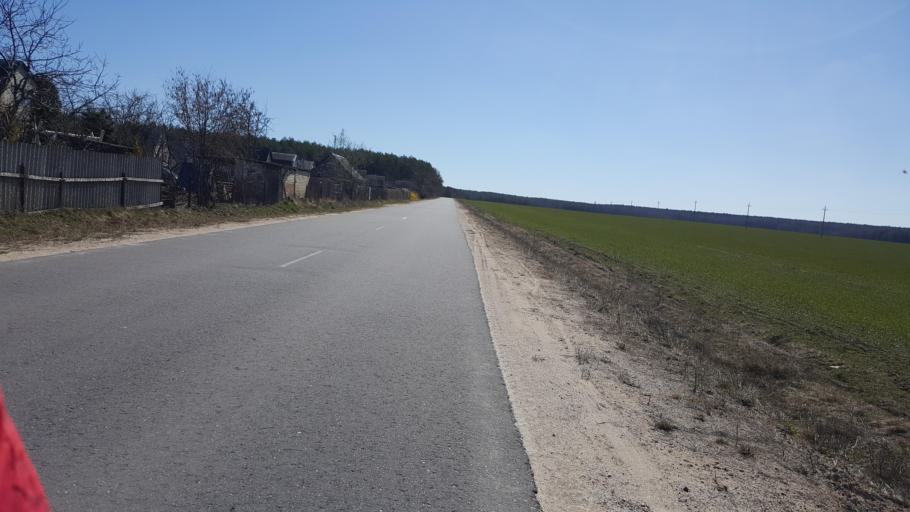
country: BY
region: Brest
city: Kamyanyets
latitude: 52.3673
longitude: 23.8032
